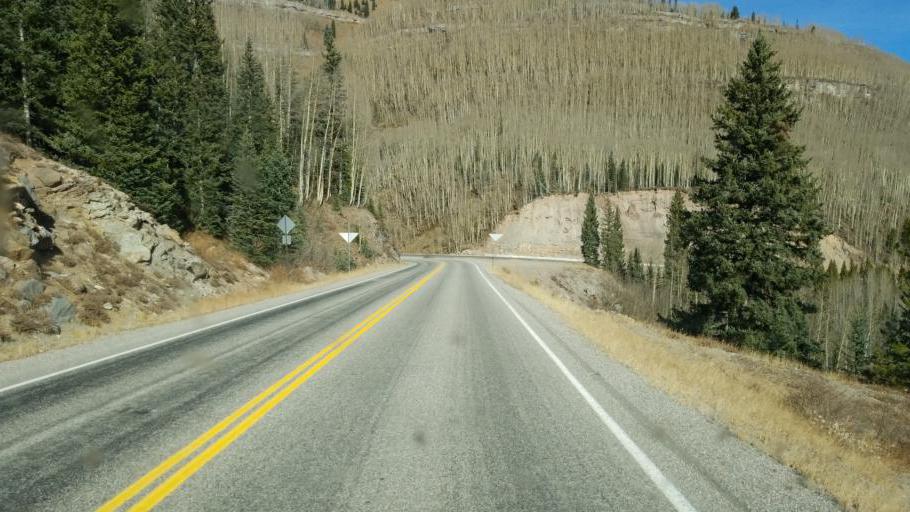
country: US
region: Colorado
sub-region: San Juan County
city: Silverton
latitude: 37.7163
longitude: -107.7551
